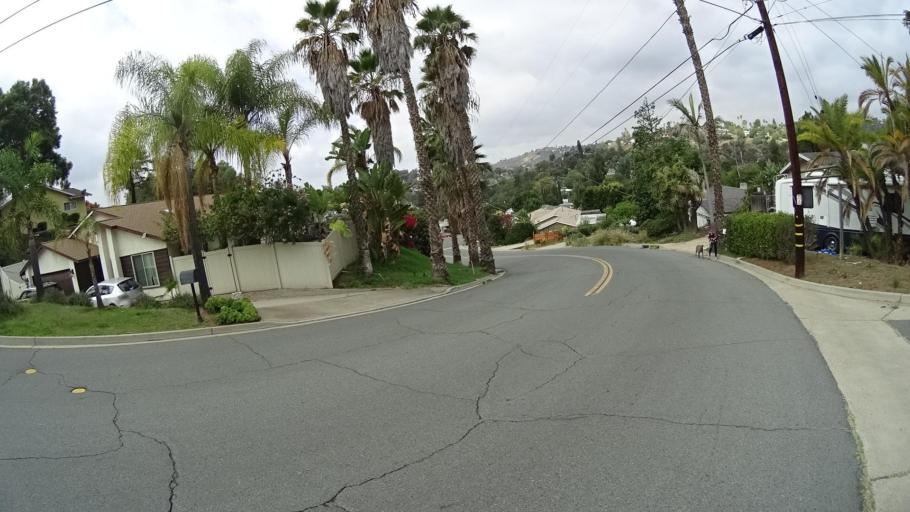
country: US
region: California
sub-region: San Diego County
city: Spring Valley
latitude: 32.7528
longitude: -116.9966
